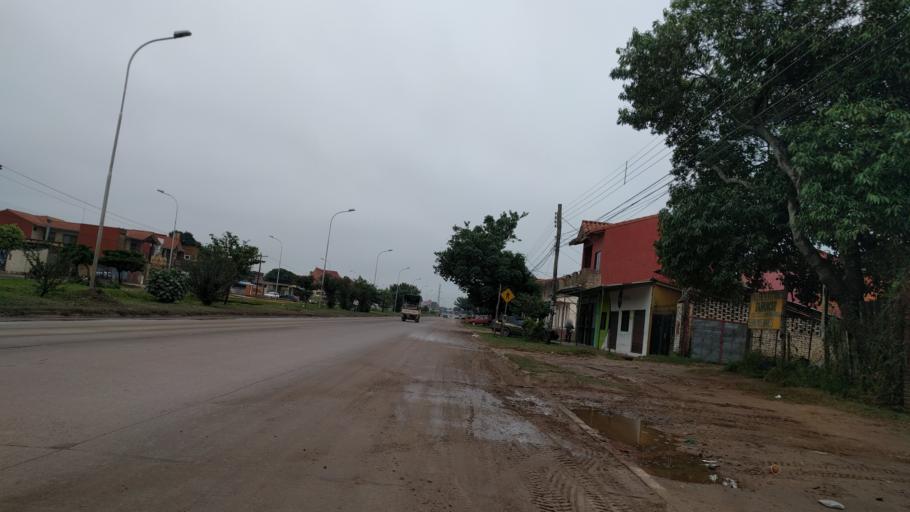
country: BO
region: Santa Cruz
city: Santa Cruz de la Sierra
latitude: -17.8313
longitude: -63.1776
